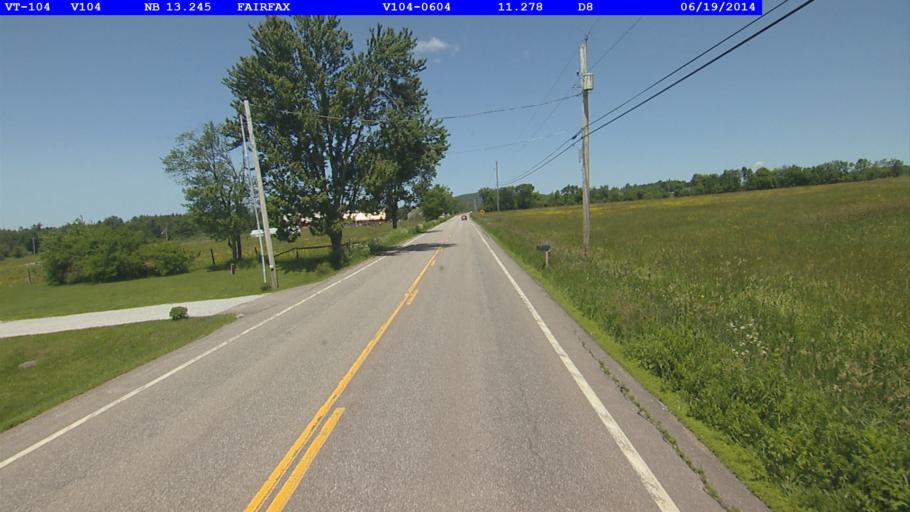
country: US
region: Vermont
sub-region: Franklin County
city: Saint Albans
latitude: 44.7464
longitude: -73.0519
